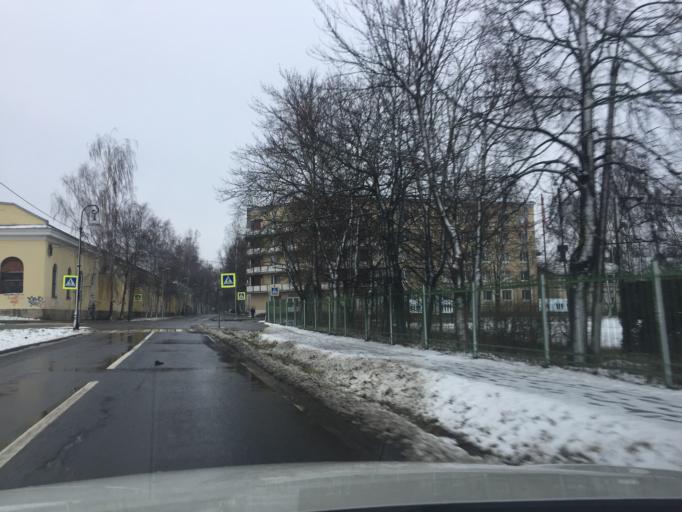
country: RU
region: St.-Petersburg
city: Pushkin
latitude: 59.7061
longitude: 30.3953
